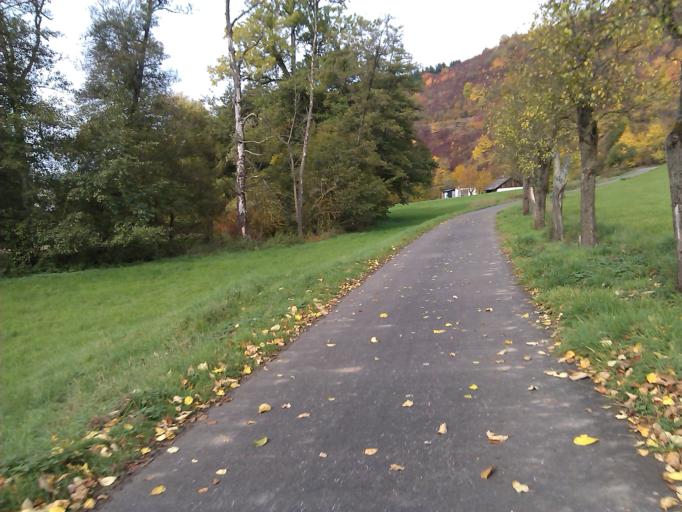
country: DE
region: Rheinland-Pfalz
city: Lohnweiler
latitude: 49.6240
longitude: 7.6113
